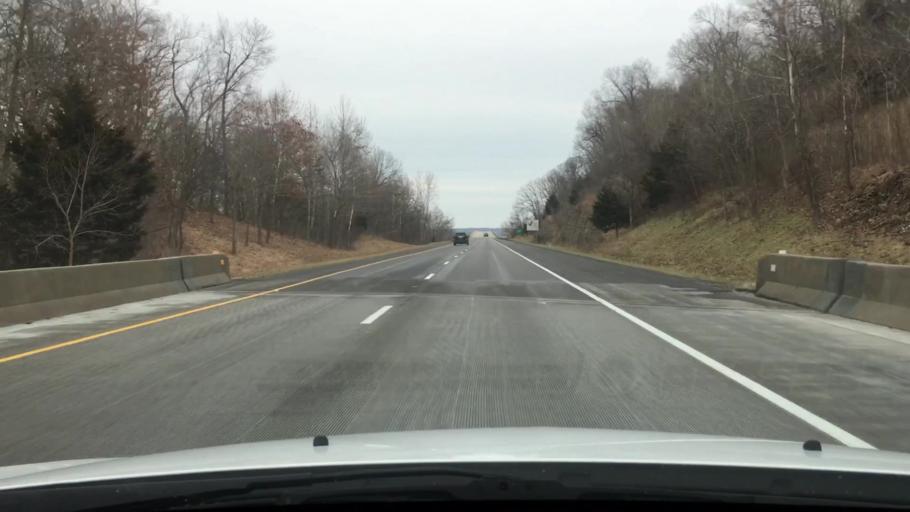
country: US
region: Illinois
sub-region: Pike County
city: Griggsville
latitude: 39.6838
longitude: -90.6488
